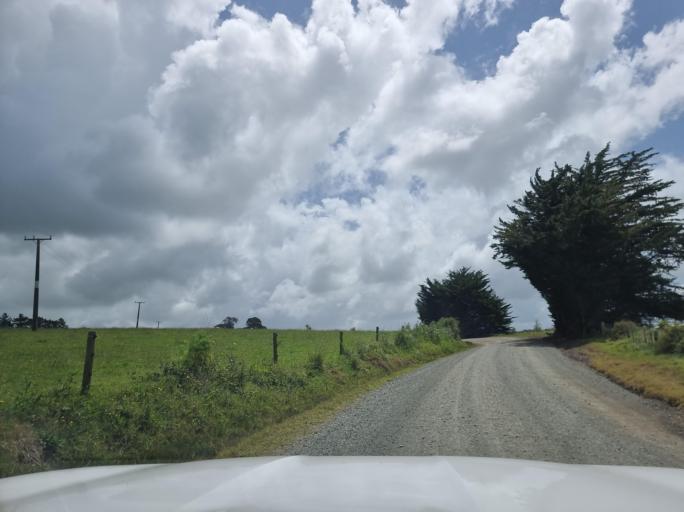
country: NZ
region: Northland
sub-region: Kaipara District
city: Dargaville
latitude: -36.1005
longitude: 174.1317
